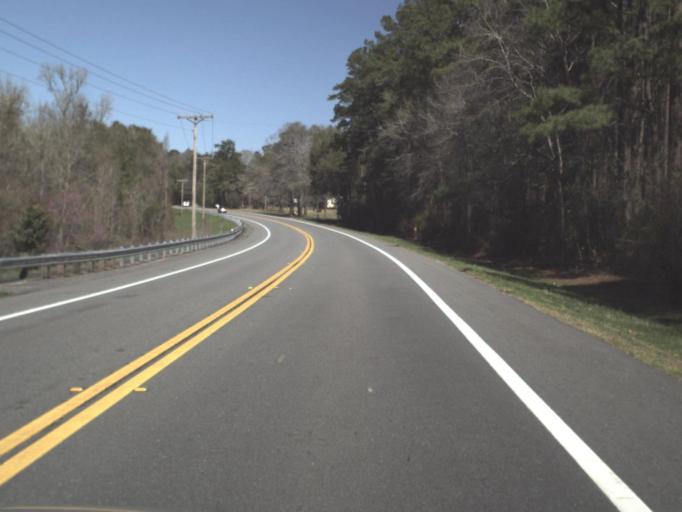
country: US
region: Florida
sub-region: Gadsden County
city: Quincy
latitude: 30.5019
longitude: -84.6085
